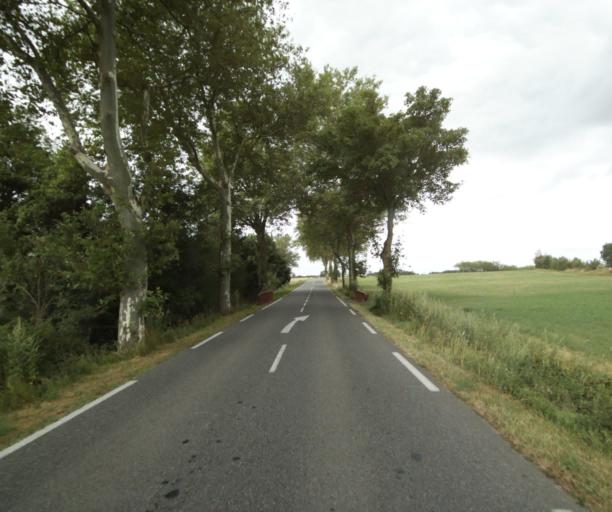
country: FR
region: Midi-Pyrenees
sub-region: Departement du Tarn
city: Soreze
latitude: 43.4614
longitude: 2.0794
